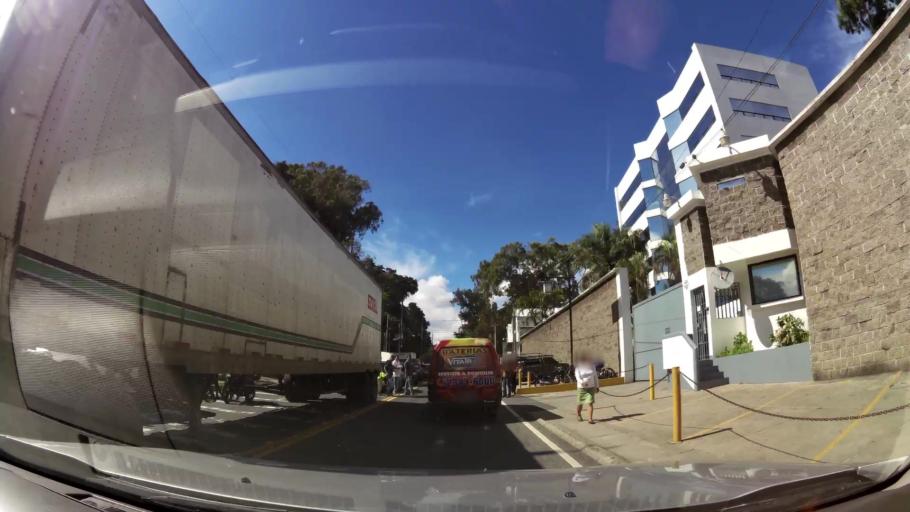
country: GT
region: Guatemala
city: Mixco
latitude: 14.6323
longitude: -90.5621
